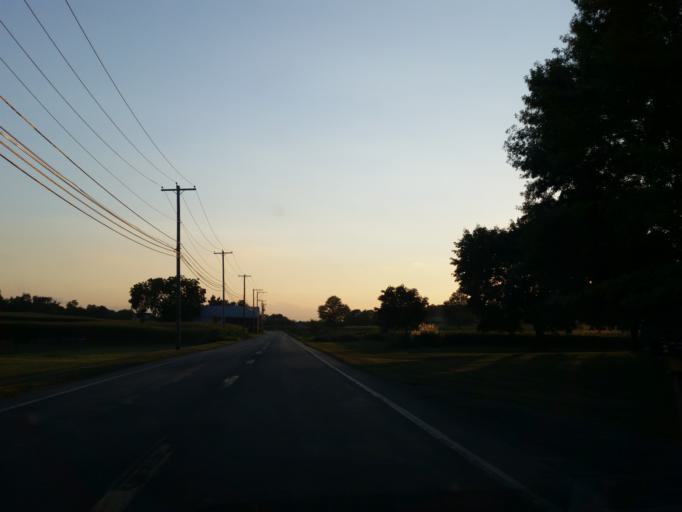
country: US
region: Pennsylvania
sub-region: Lebanon County
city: Richland
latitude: 40.3007
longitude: -76.2723
